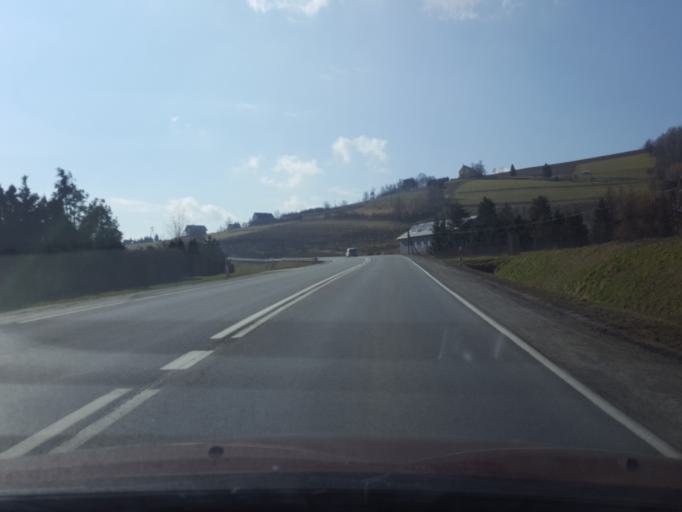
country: PL
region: Lesser Poland Voivodeship
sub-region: Powiat nowosadecki
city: Lososina Dolna
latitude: 49.7294
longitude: 20.6390
